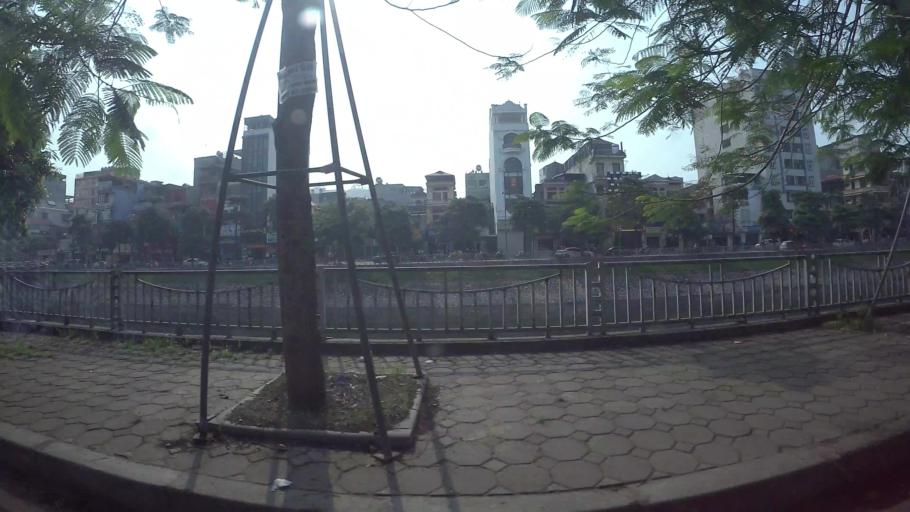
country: VN
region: Ha Noi
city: Thanh Xuan
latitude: 20.9934
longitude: 105.8145
